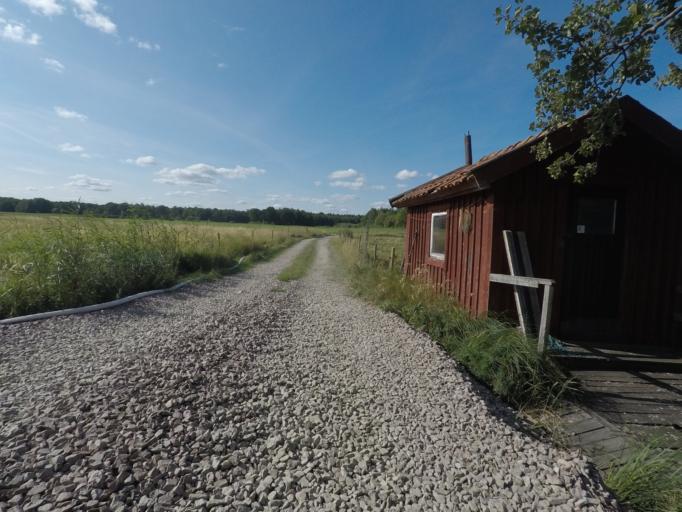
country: SE
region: Soedermanland
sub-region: Eskilstuna Kommun
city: Kvicksund
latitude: 59.4392
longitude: 16.2788
